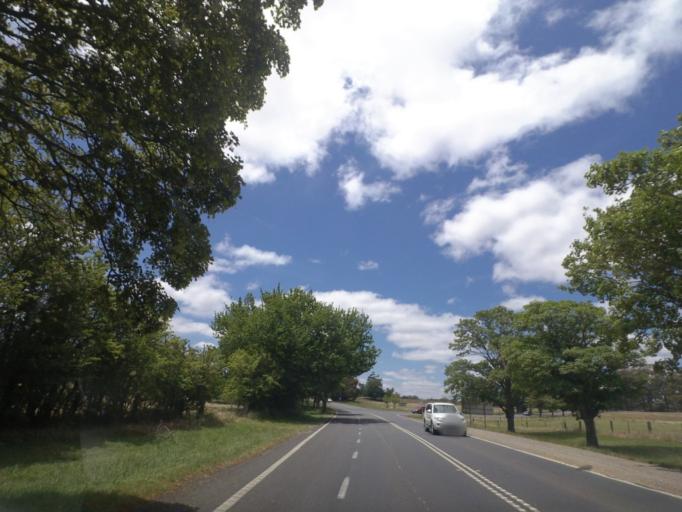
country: AU
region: Victoria
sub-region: Mount Alexander
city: Castlemaine
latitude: -37.3356
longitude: 144.1645
